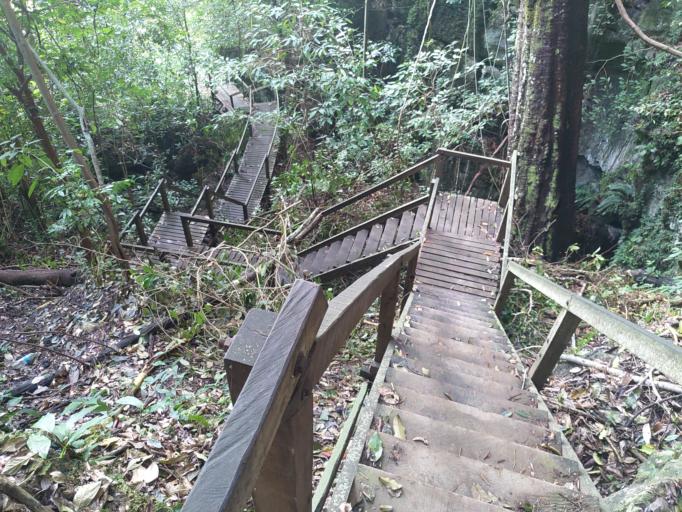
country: MY
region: Sarawak
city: Miri
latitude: 3.8115
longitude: 113.7875
